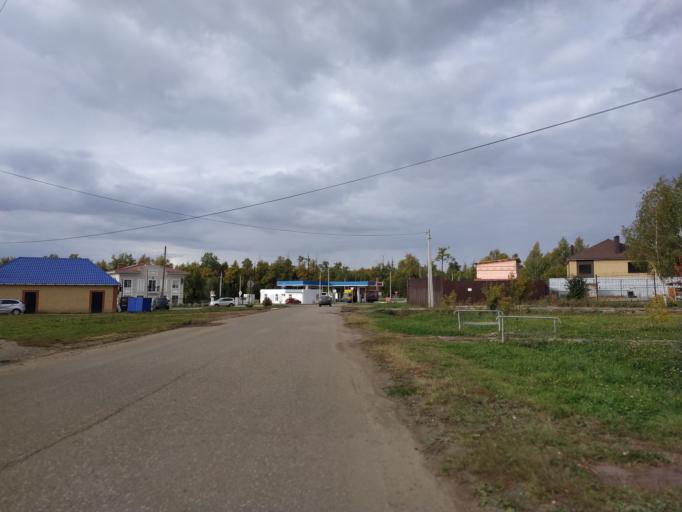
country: RU
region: Chuvashia
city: Ishley
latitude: 56.1320
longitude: 47.0869
